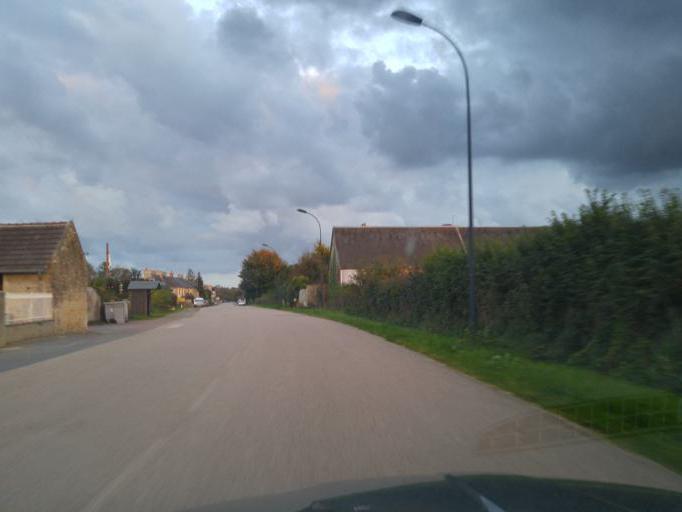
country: FR
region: Lower Normandy
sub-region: Departement du Calvados
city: Grandcamp-Maisy
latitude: 49.3409
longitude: -0.9698
